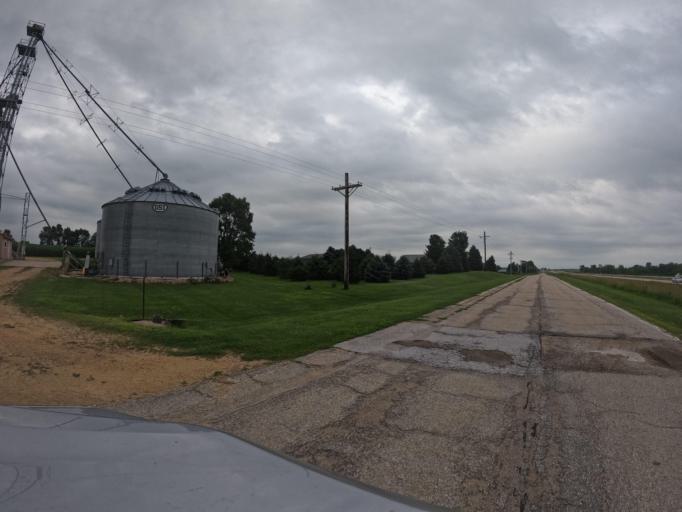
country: US
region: Iowa
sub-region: Clinton County
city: De Witt
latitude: 41.8871
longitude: -90.5838
